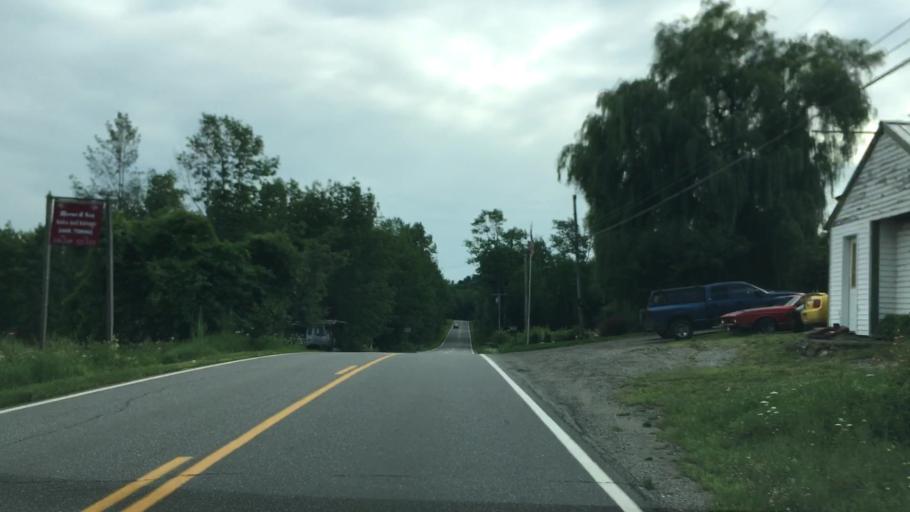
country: US
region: Maine
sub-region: Waldo County
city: Belfast
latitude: 44.3572
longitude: -69.0491
